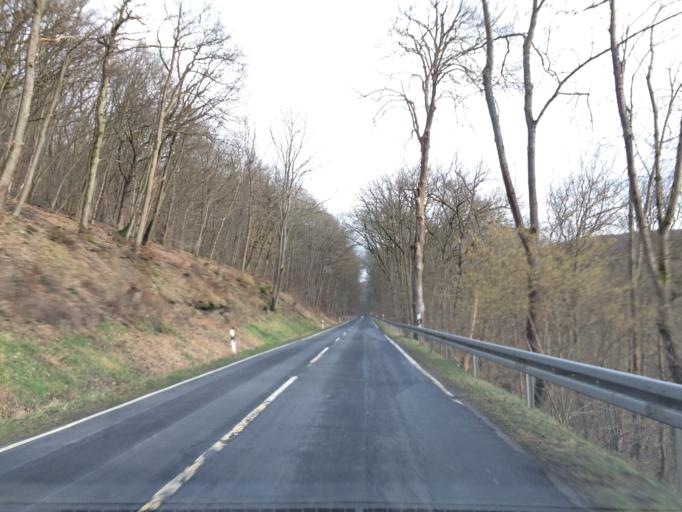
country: DE
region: Hesse
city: Weilmunster
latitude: 50.3696
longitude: 8.3882
